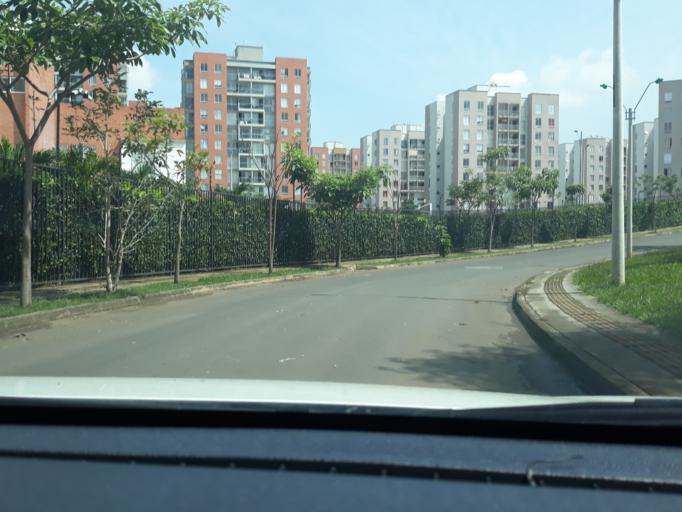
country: CO
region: Valle del Cauca
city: Cali
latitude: 3.3675
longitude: -76.5111
